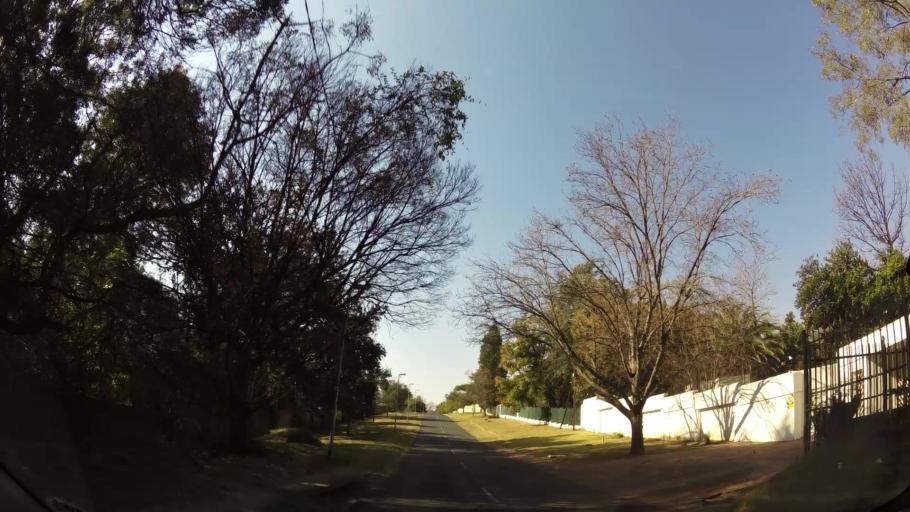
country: ZA
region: Gauteng
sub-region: City of Johannesburg Metropolitan Municipality
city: Diepsloot
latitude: -26.0656
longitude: 28.0090
